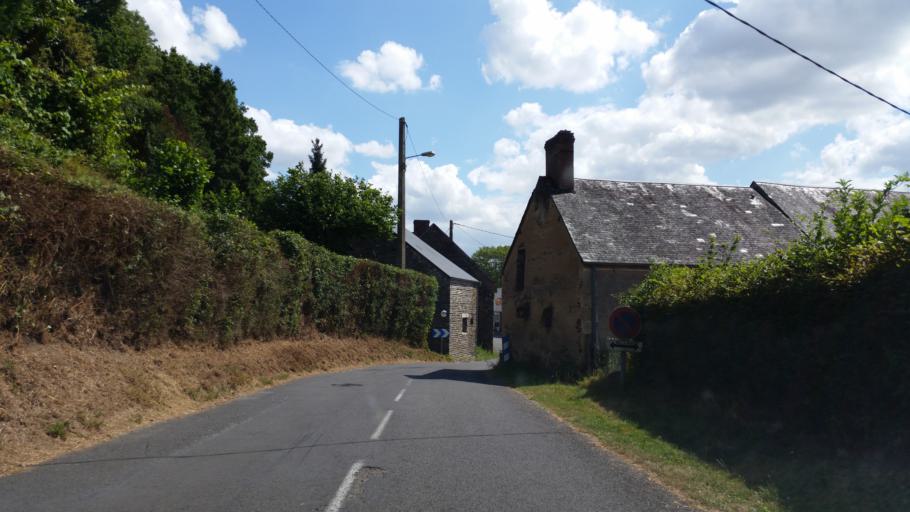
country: FR
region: Lower Normandy
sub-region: Departement du Calvados
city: Clecy
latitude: 48.8580
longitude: -0.3984
